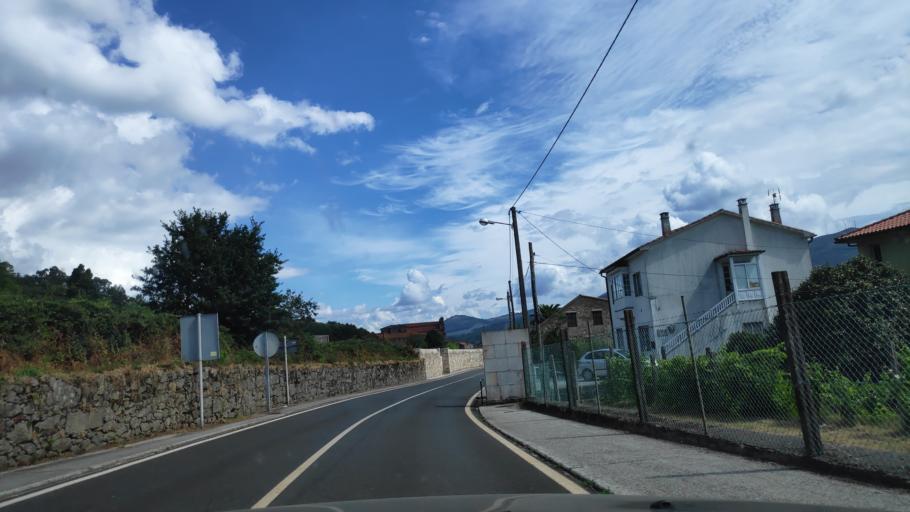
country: ES
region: Galicia
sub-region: Provincia da Coruna
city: Padron
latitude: 42.7353
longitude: -8.6655
